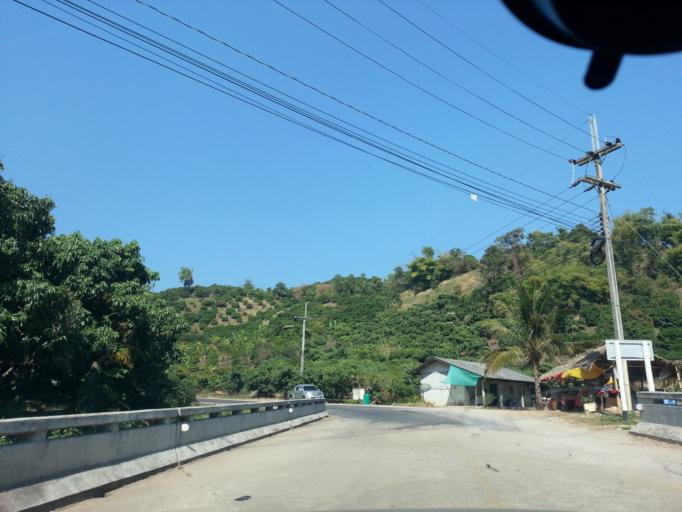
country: TH
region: Chiang Mai
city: Chai Prakan
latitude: 19.8221
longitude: 99.0995
